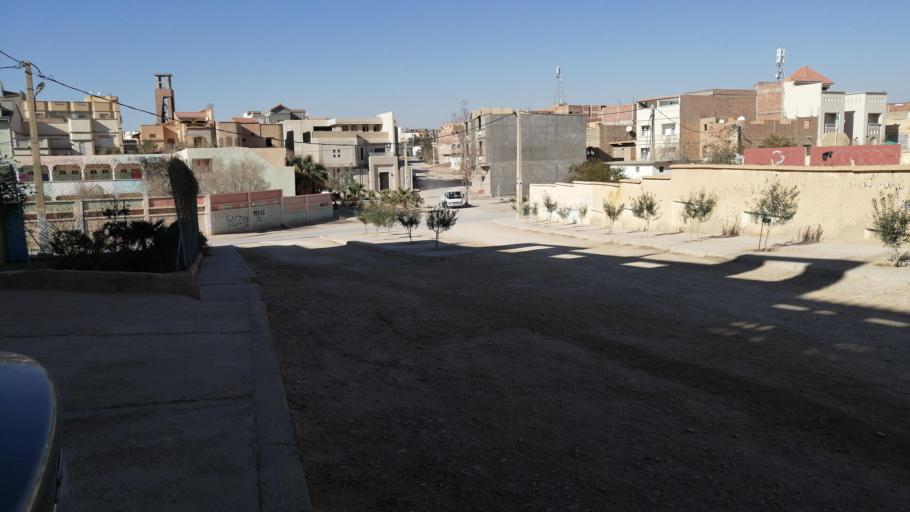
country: DZ
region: Biskra
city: Biskra
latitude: 34.8617
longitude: 5.7155
